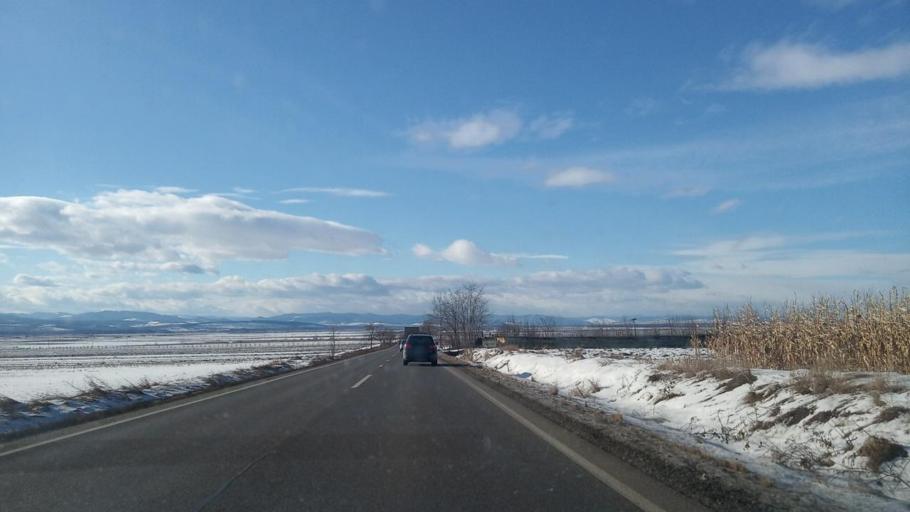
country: RO
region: Suceava
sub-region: Comuna Radaseni
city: Radaseni
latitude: 47.4516
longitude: 26.2505
